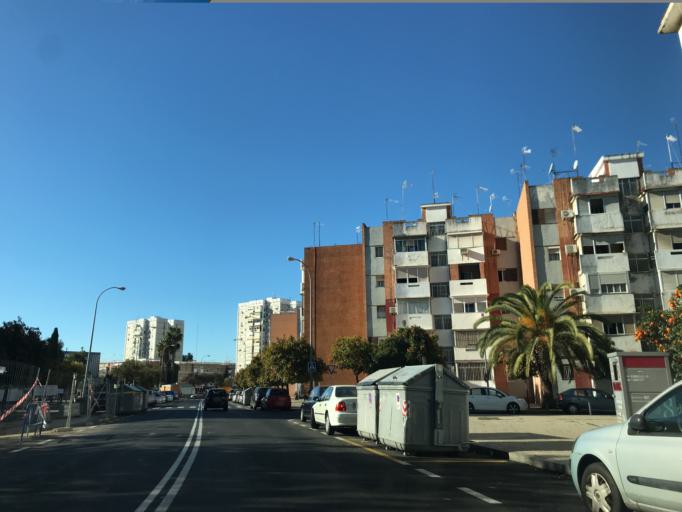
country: ES
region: Andalusia
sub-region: Provincia de Sevilla
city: Sevilla
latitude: 37.3998
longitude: -5.9581
